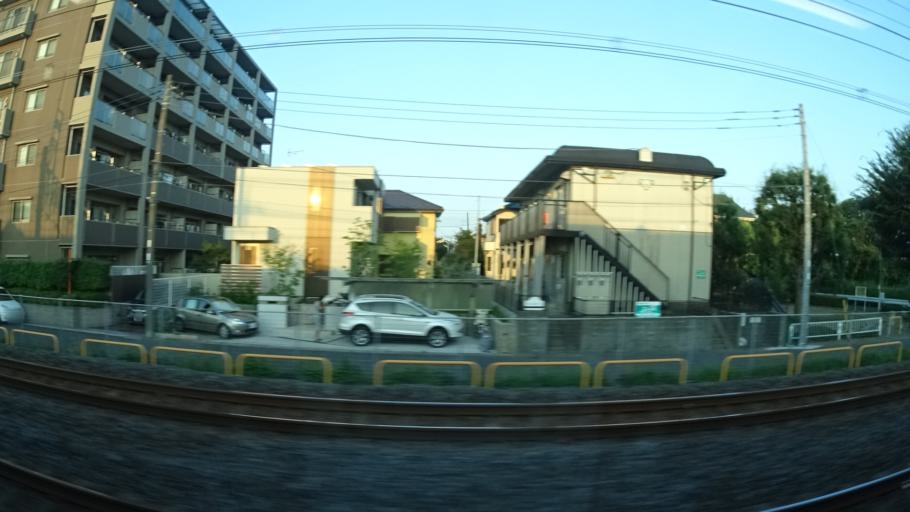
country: JP
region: Chiba
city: Nagareyama
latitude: 35.8220
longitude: 139.9199
